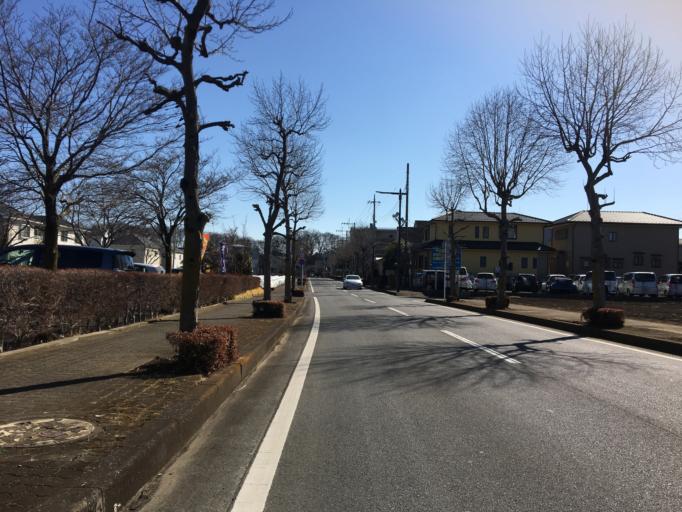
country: JP
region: Saitama
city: Oi
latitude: 35.8516
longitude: 139.5184
